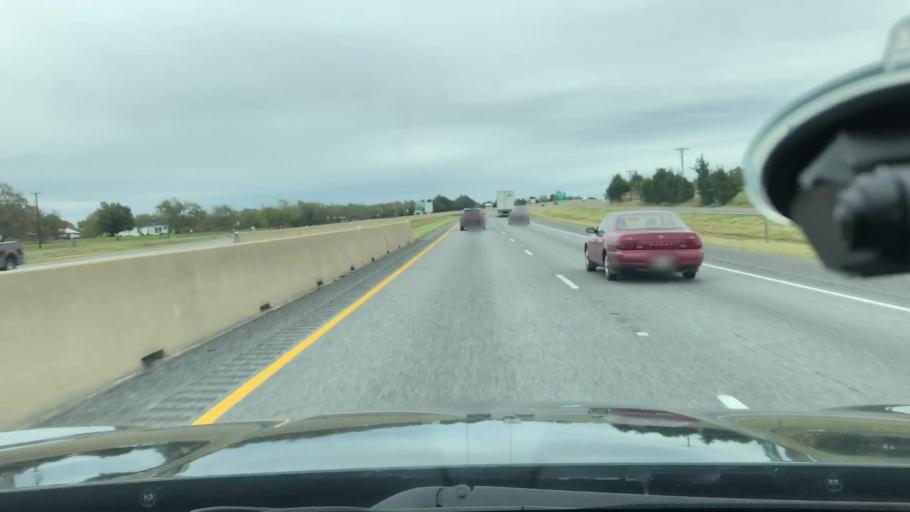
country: US
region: Texas
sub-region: Hunt County
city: Greenville
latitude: 33.1326
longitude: -96.0177
